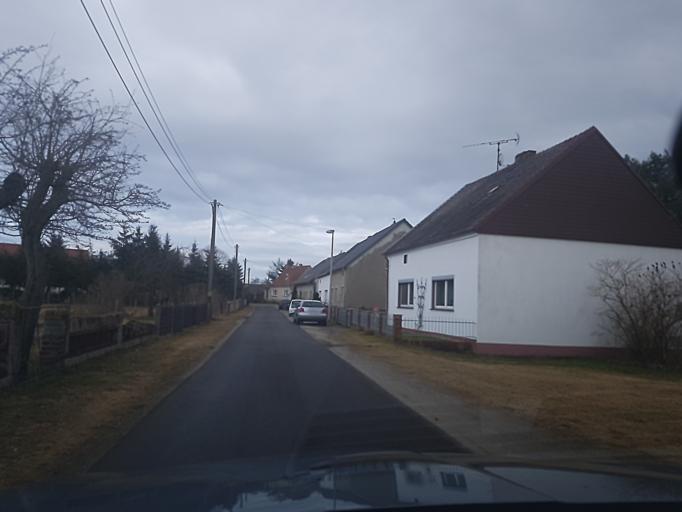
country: DE
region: Brandenburg
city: Sonnewalde
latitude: 51.6845
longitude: 13.6491
